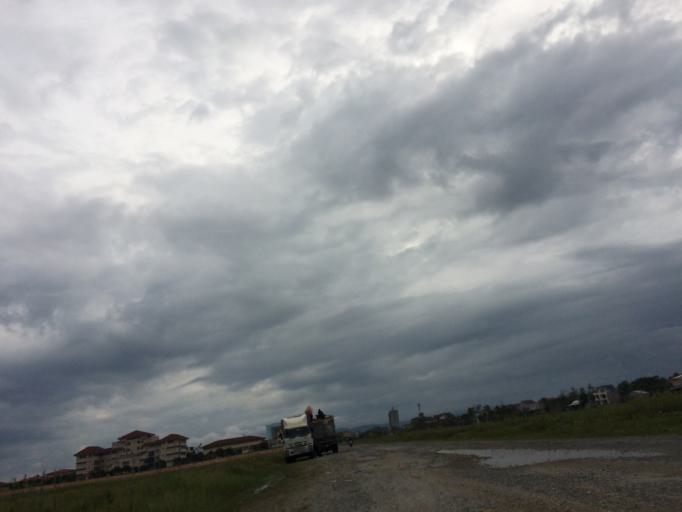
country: VN
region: Ha Tinh
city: Ha Tinh
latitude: 18.3599
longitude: 105.8953
